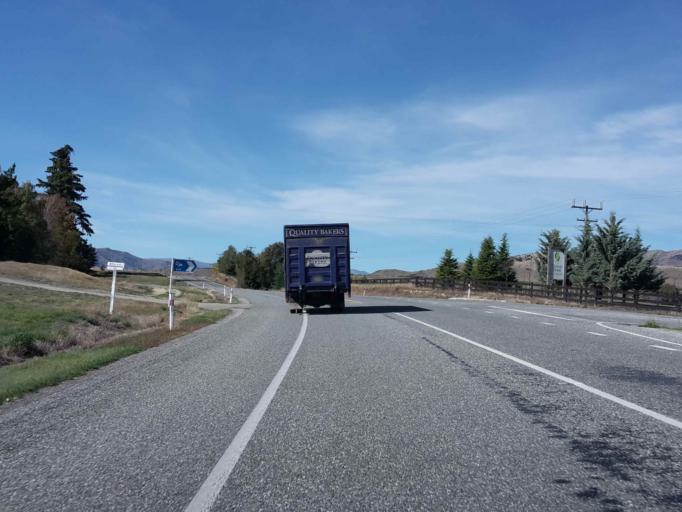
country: NZ
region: Otago
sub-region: Queenstown-Lakes District
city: Wanaka
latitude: -44.7166
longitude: 169.2153
